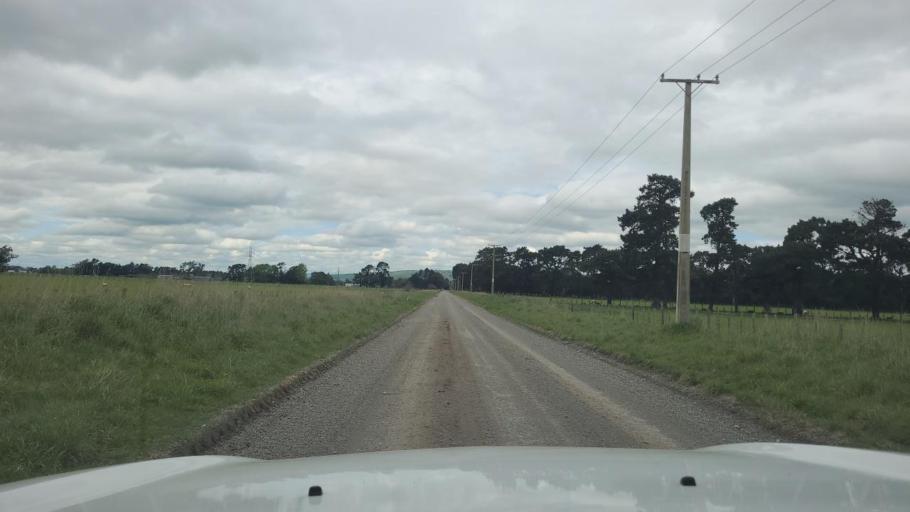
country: NZ
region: Wellington
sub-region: Masterton District
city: Masterton
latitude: -41.1190
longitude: 175.4251
